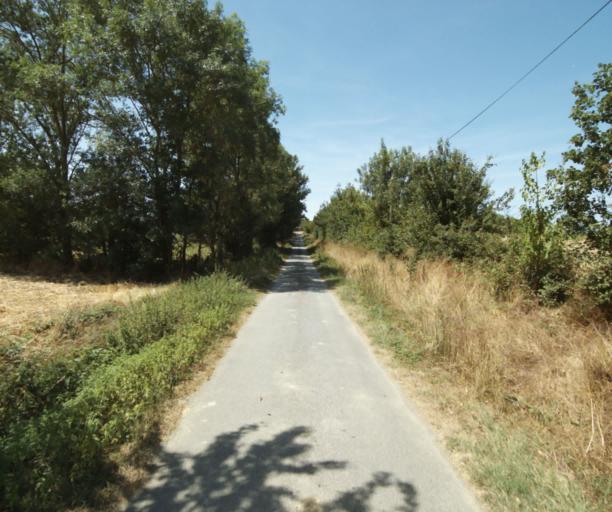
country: FR
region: Midi-Pyrenees
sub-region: Departement de la Haute-Garonne
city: Revel
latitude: 43.5033
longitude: 2.0353
